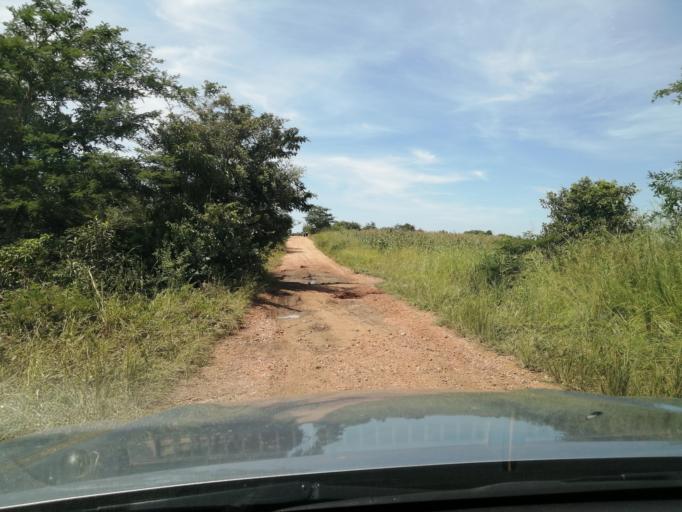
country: ZM
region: Central
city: Chibombo
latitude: -15.0109
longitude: 27.8284
